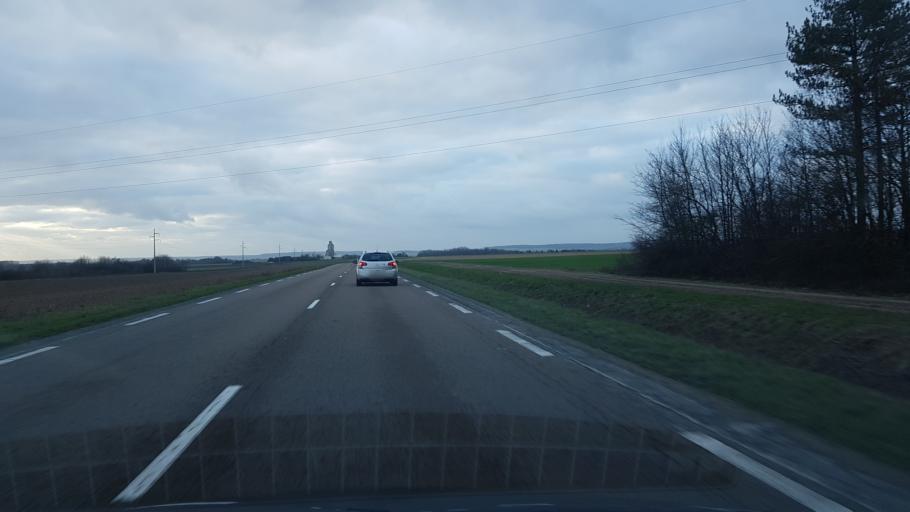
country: FR
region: Champagne-Ardenne
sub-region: Departement de la Marne
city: Connantre
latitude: 48.7279
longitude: 3.8751
